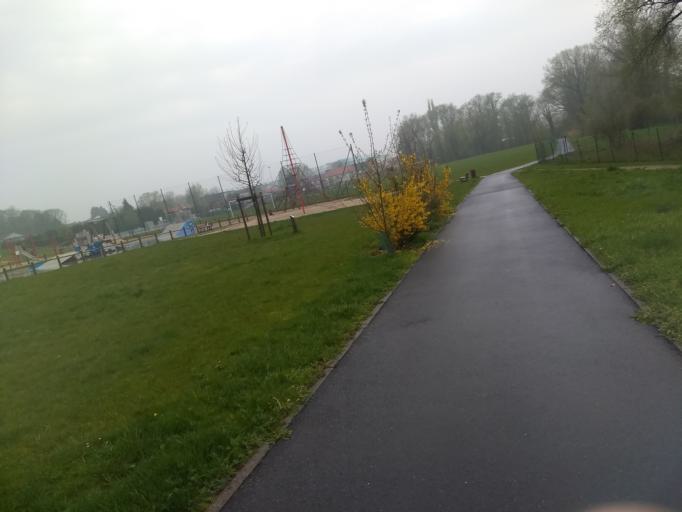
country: FR
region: Nord-Pas-de-Calais
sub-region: Departement du Pas-de-Calais
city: Biache-Saint-Vaast
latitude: 50.3089
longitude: 2.9549
